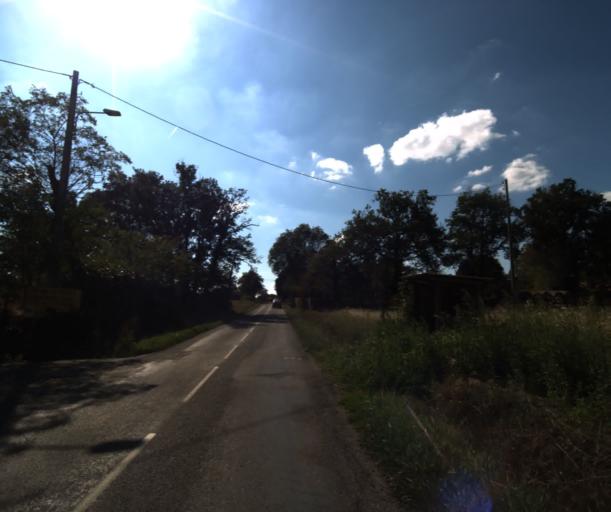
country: FR
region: Midi-Pyrenees
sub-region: Departement de la Haute-Garonne
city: Saint-Lys
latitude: 43.5044
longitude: 1.2014
